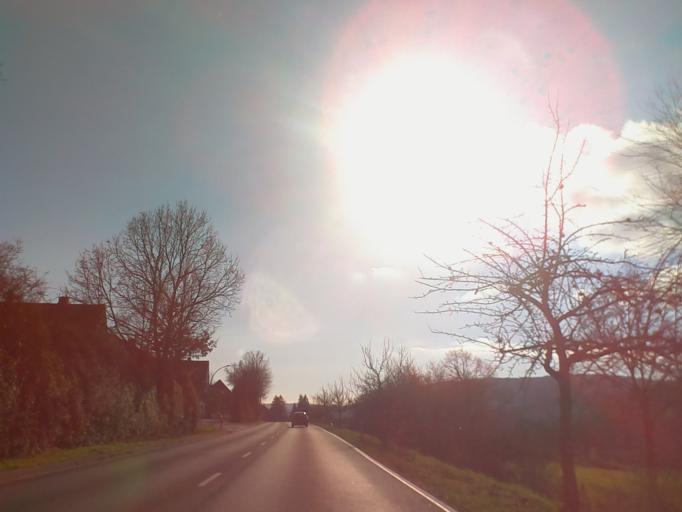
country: DE
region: Bavaria
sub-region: Regierungsbezirk Unterfranken
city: Bad Kissingen
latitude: 50.2263
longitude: 10.0688
